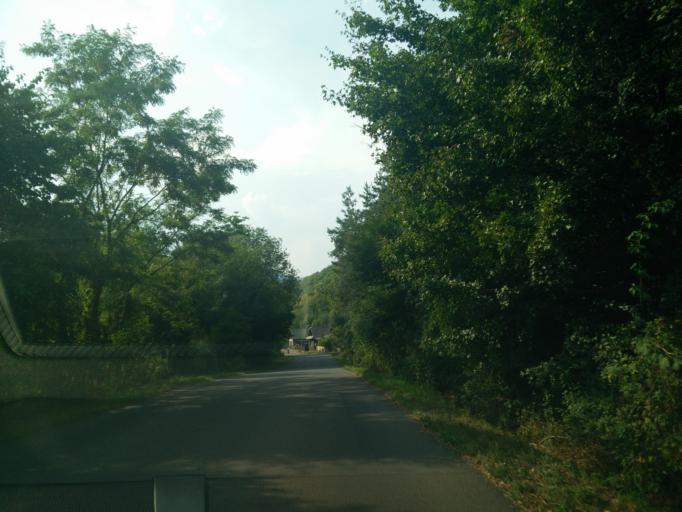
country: SK
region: Banskobystricky
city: Zarnovica
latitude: 48.5238
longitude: 18.7563
